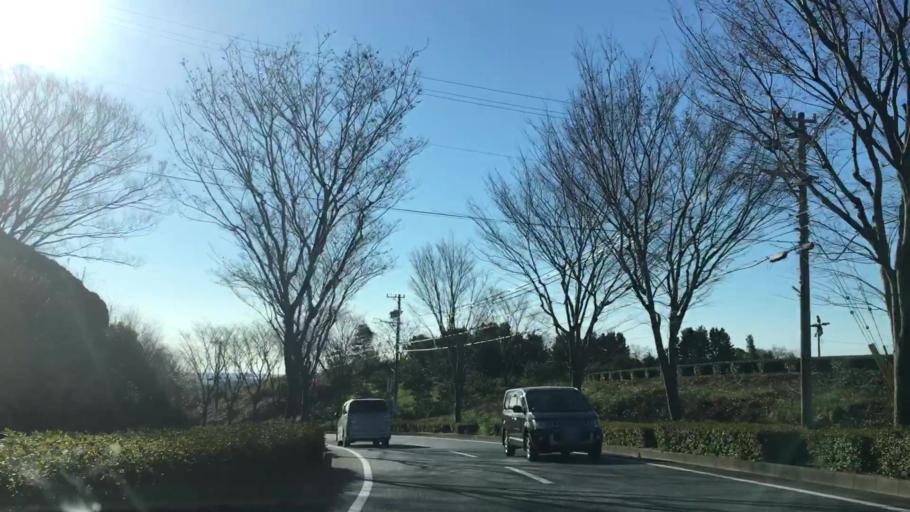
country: JP
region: Shizuoka
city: Hamakita
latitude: 34.8021
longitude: 137.7450
